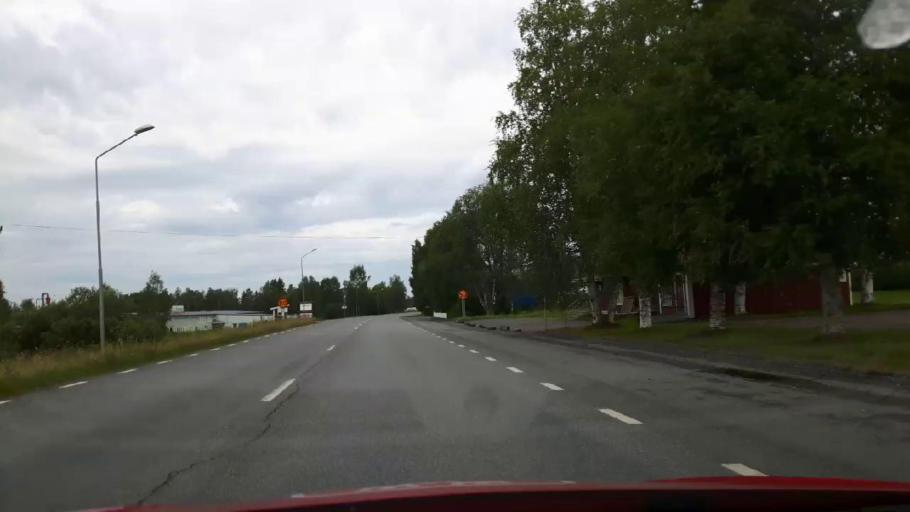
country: SE
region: Jaemtland
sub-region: Stroemsunds Kommun
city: Stroemsund
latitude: 63.5753
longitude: 15.3538
